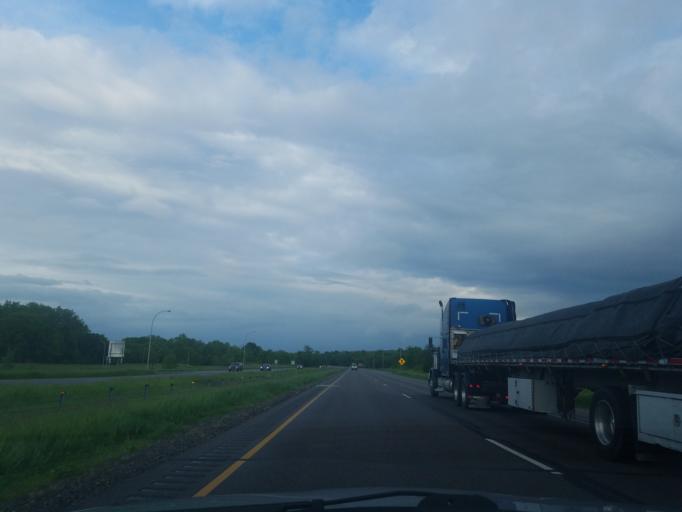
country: US
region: Minnesota
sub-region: Stearns County
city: Avon
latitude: 45.6039
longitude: -94.4808
